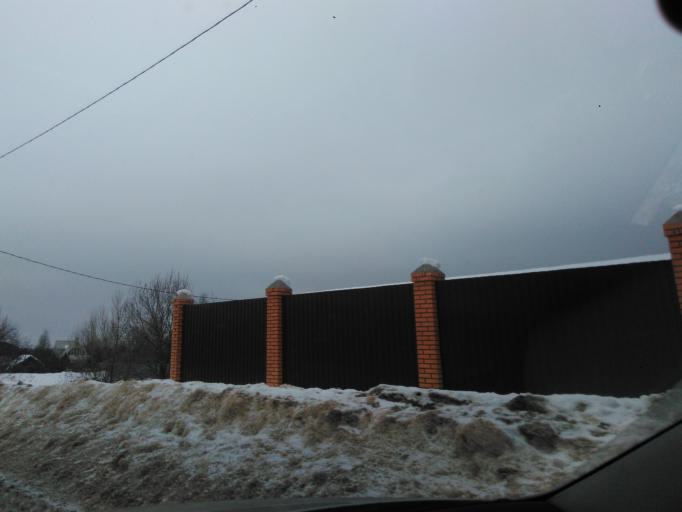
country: RU
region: Moskovskaya
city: Podosinki
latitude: 56.2765
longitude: 37.5941
